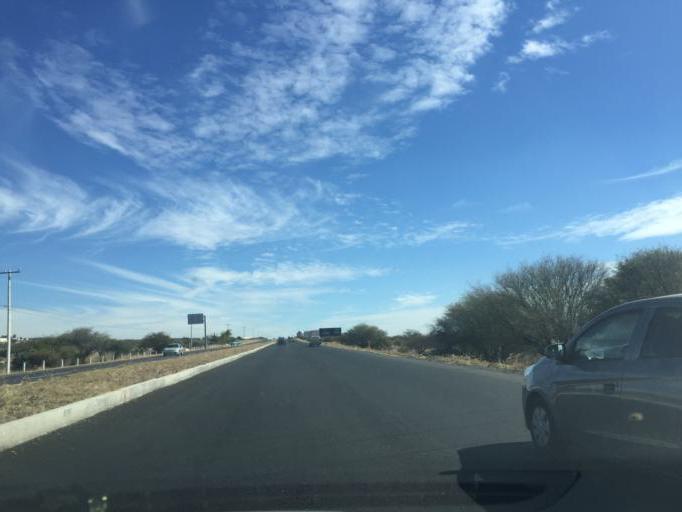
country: MX
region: Queretaro
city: San Nicolas
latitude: 20.5015
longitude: -99.9236
